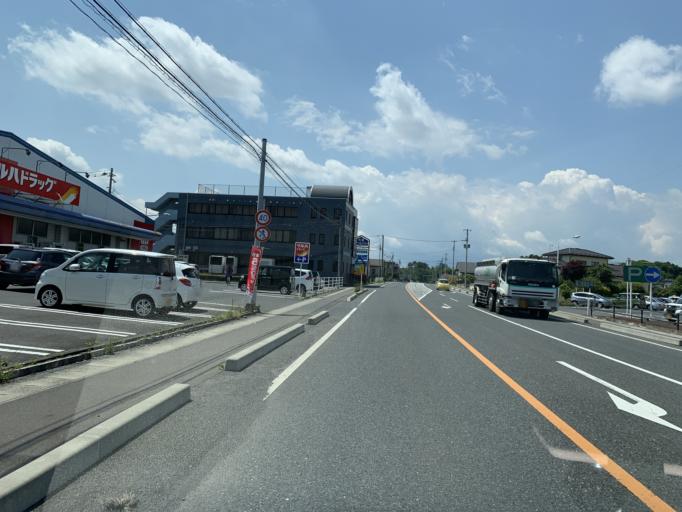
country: JP
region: Miyagi
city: Kogota
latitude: 38.5430
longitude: 141.0594
